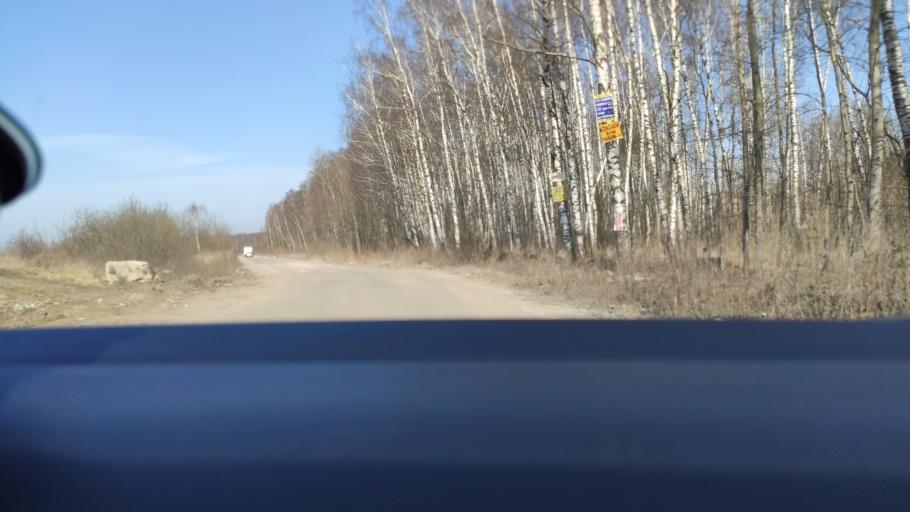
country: RU
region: Moskovskaya
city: Elektrostal'
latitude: 55.7682
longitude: 38.3855
